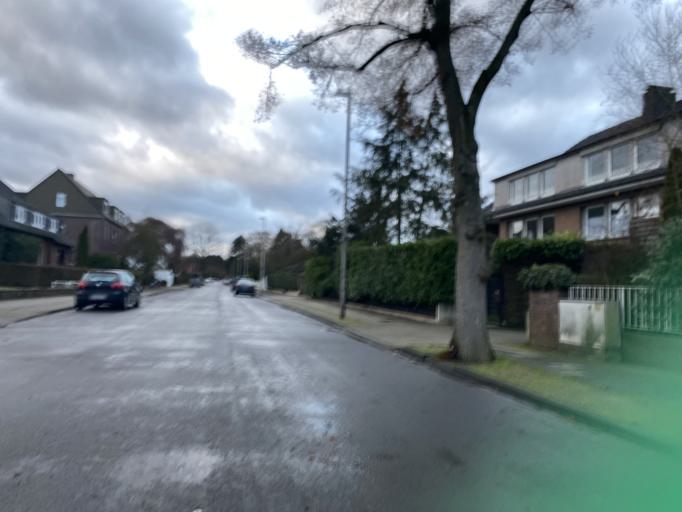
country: DE
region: North Rhine-Westphalia
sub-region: Regierungsbezirk Arnsberg
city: Hamm
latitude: 51.6937
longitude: 7.8588
